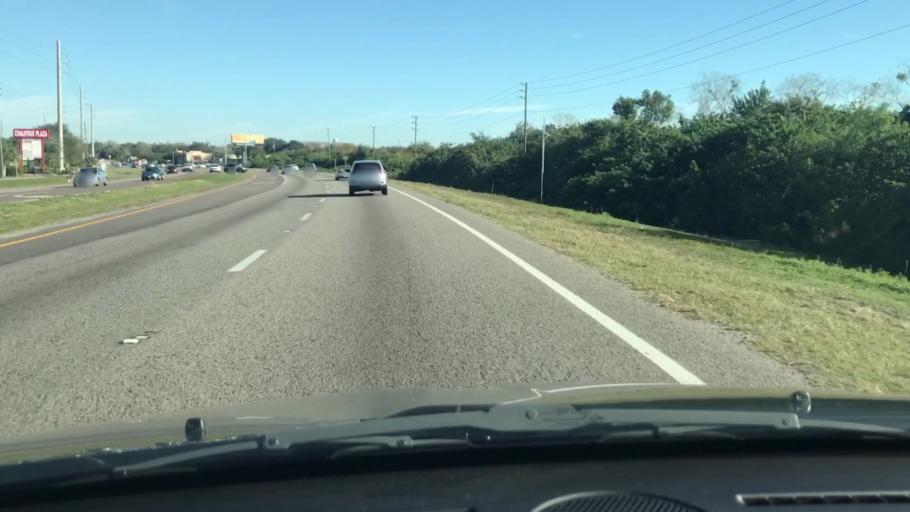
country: US
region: Florida
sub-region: Osceola County
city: Kissimmee
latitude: 28.2786
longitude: -81.4169
